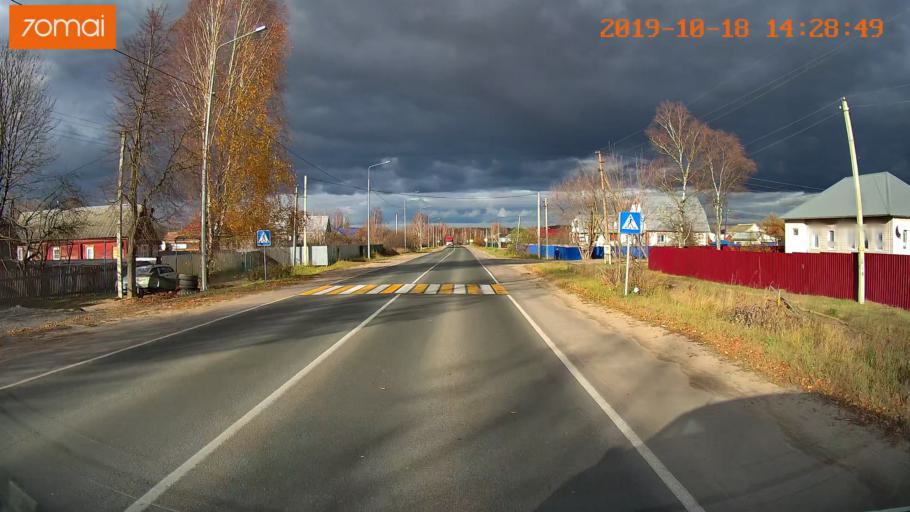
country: RU
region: Rjazan
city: Tuma
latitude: 55.1513
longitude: 40.5549
